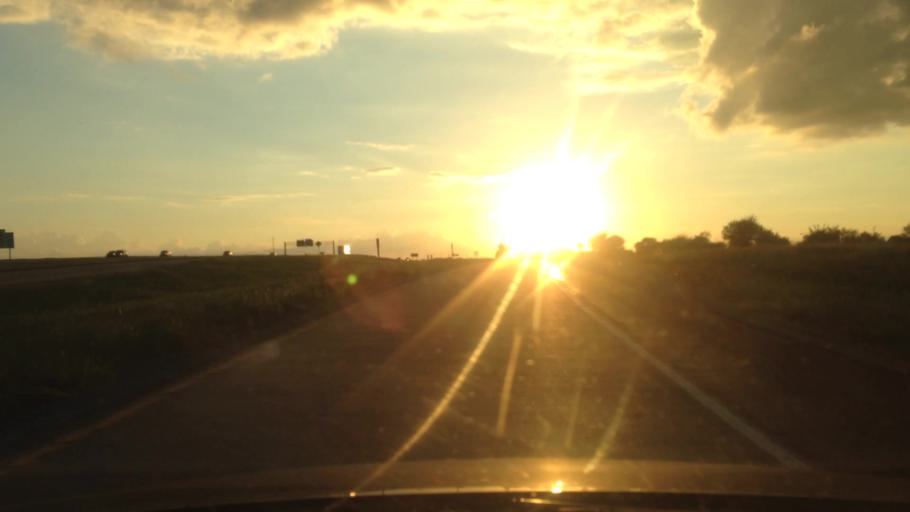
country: US
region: Texas
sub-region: Tarrant County
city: Benbrook
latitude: 32.6935
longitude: -97.4942
